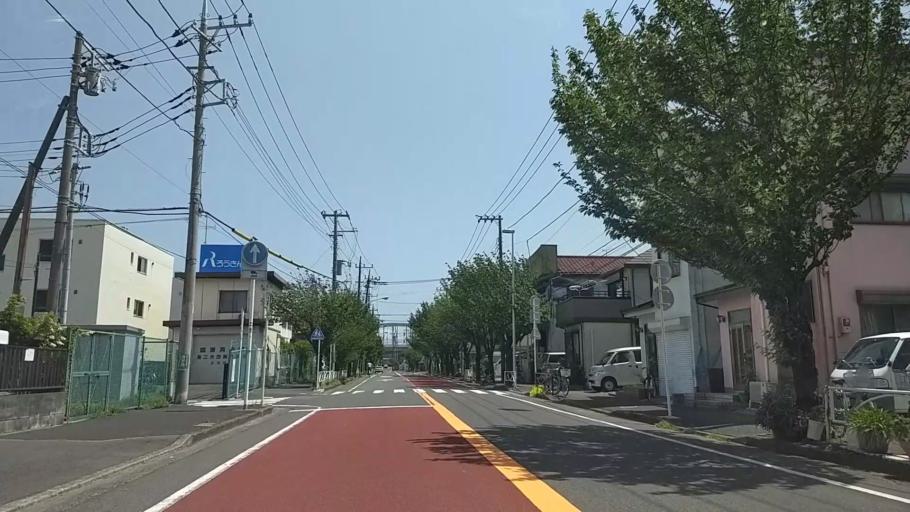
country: JP
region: Kanagawa
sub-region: Kawasaki-shi
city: Kawasaki
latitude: 35.5183
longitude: 139.7206
